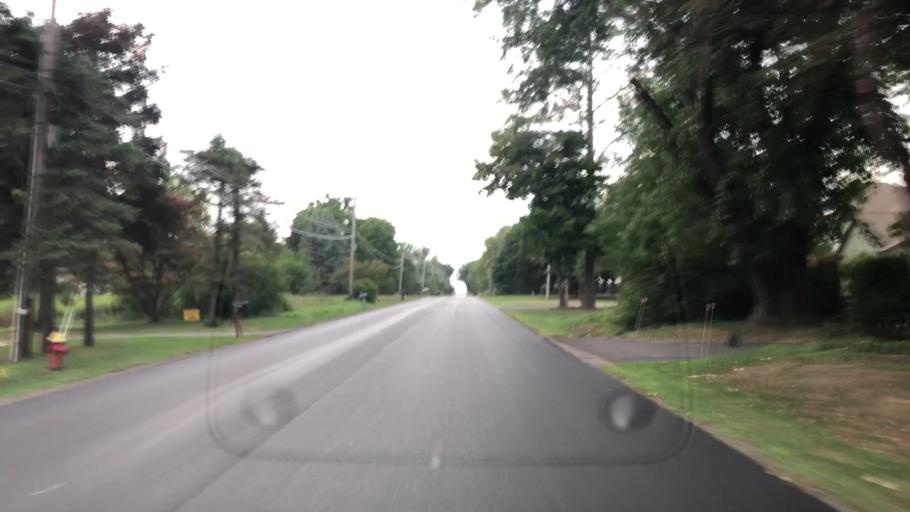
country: US
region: New York
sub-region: Erie County
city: Billington Heights
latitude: 42.8099
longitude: -78.6059
